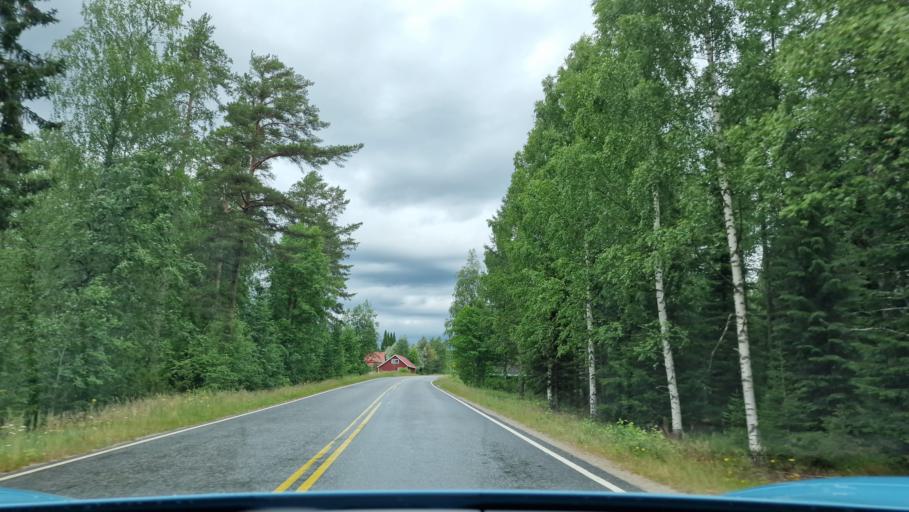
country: FI
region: Southern Ostrobothnia
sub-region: Jaerviseutu
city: Soini
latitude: 62.6951
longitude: 24.4576
